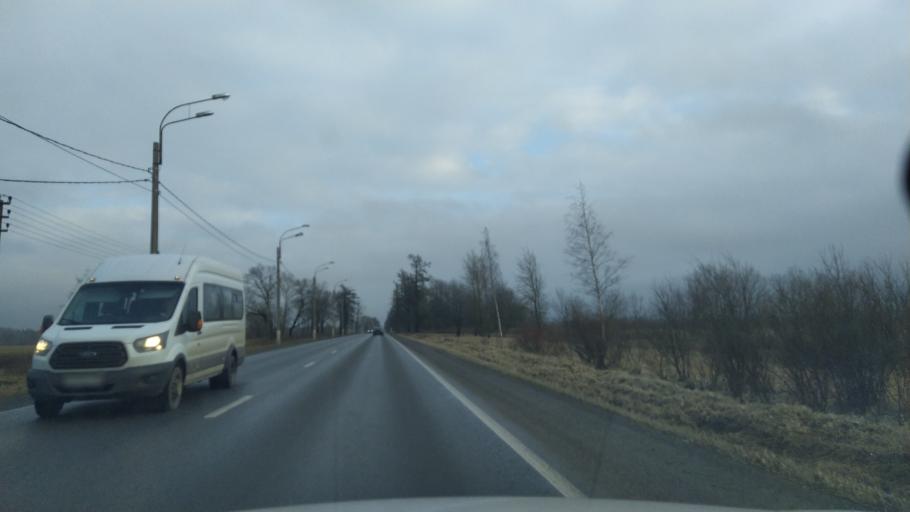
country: RU
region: St.-Petersburg
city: Aleksandrovskaya
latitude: 59.7105
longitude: 30.3182
